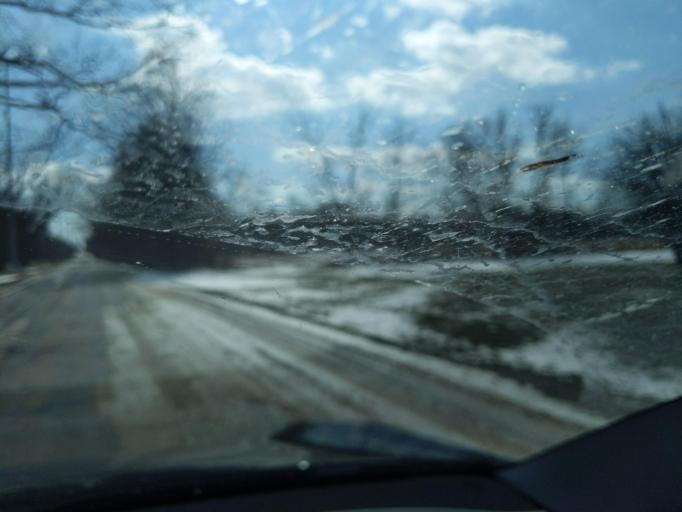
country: US
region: Michigan
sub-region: Livingston County
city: Fowlerville
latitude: 42.6324
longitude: -84.0916
